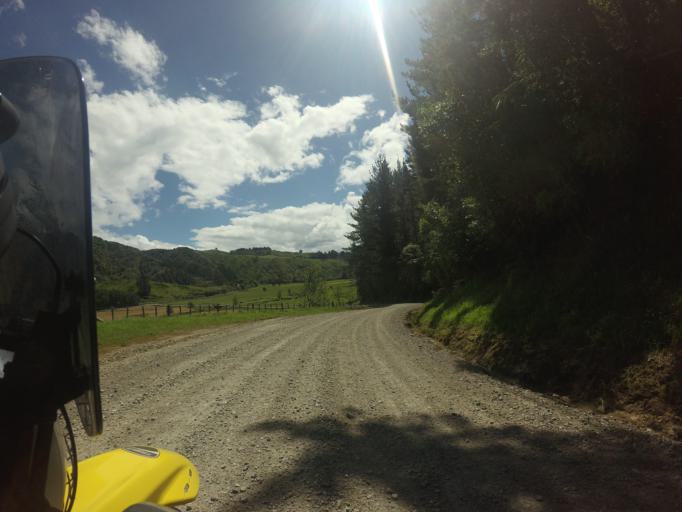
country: NZ
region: Hawke's Bay
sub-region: Wairoa District
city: Wairoa
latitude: -38.9835
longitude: 177.7011
